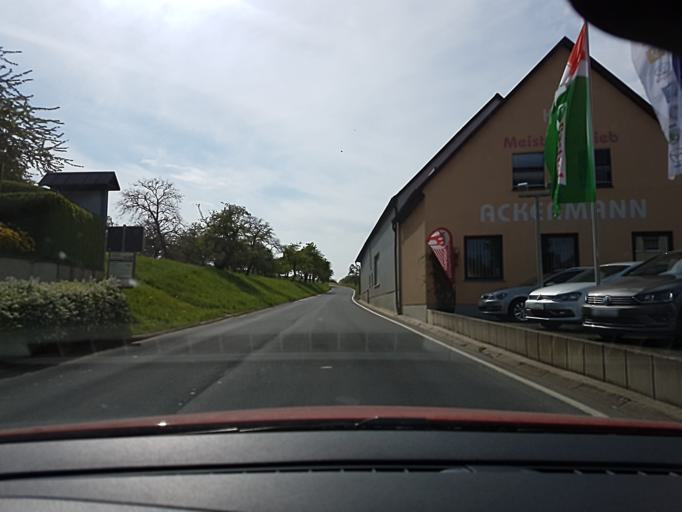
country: DE
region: Bavaria
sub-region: Regierungsbezirk Unterfranken
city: Bergtheim
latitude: 49.9278
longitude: 10.0245
